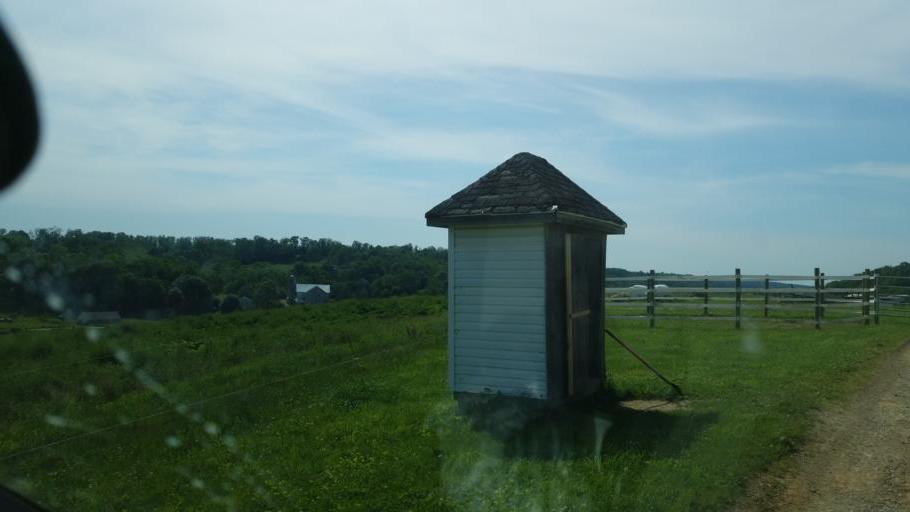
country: US
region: Ohio
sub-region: Sandusky County
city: Bellville
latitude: 40.5534
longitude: -82.3763
